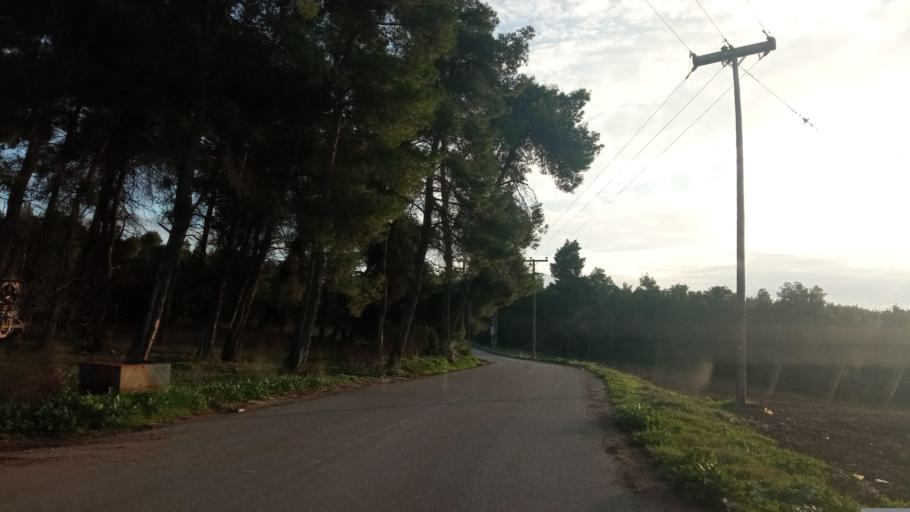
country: GR
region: Central Greece
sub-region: Nomos Evvoias
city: Kastella
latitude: 38.5645
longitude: 23.7098
